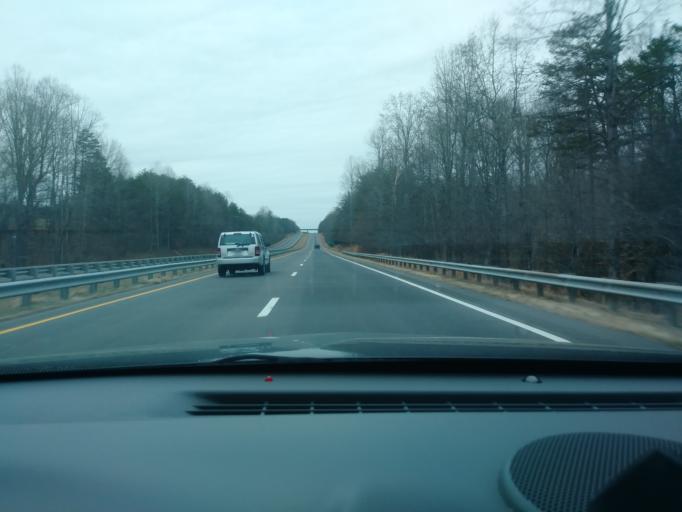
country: US
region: North Carolina
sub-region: Forsyth County
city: Lewisville
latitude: 36.1018
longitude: -80.4796
